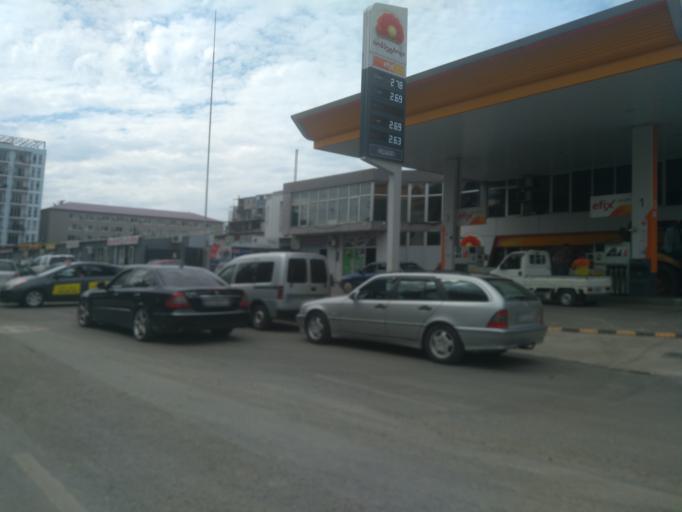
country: GE
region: Ajaria
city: Batumi
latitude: 41.6360
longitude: 41.6301
